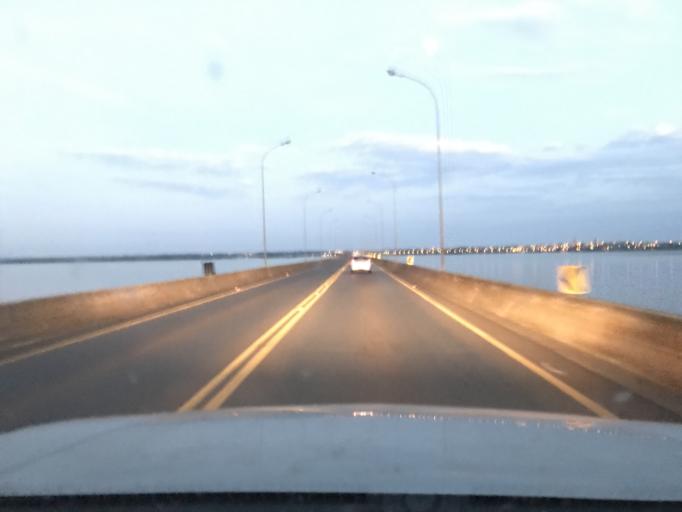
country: PY
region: Canindeyu
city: Salto del Guaira
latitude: -24.0456
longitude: -54.2710
